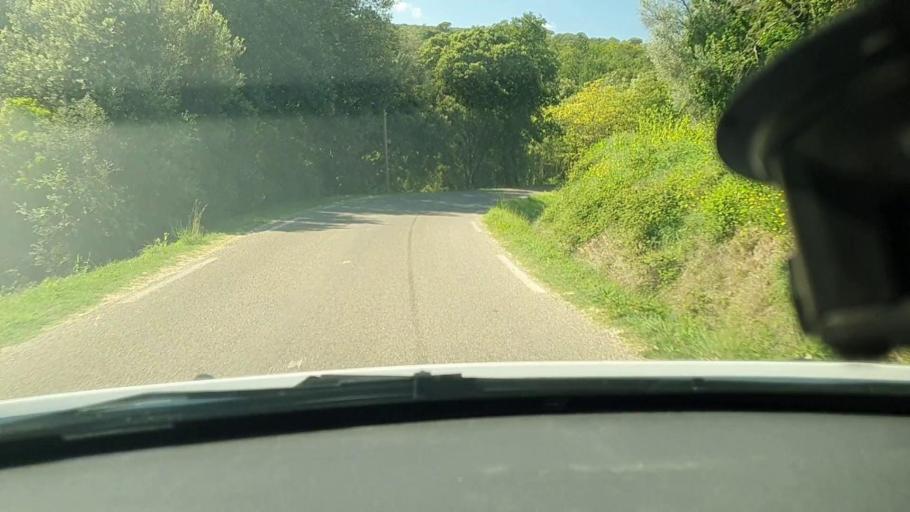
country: FR
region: Languedoc-Roussillon
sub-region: Departement du Gard
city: Sabran
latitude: 44.1880
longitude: 4.5235
